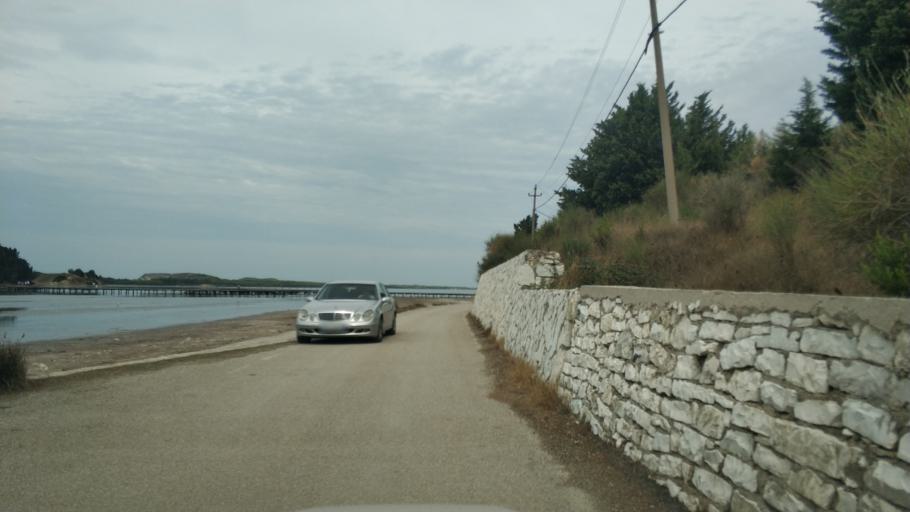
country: AL
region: Vlore
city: Vlore
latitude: 40.5163
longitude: 19.4069
